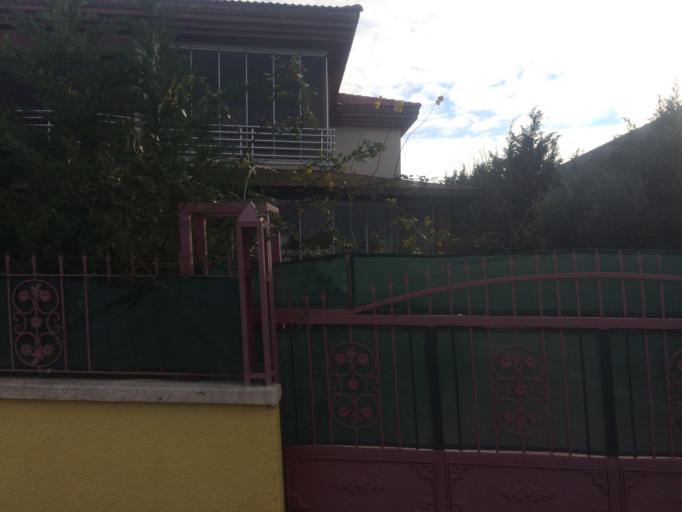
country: TR
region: Izmir
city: Karsiyaka
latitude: 38.4943
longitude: 26.9541
